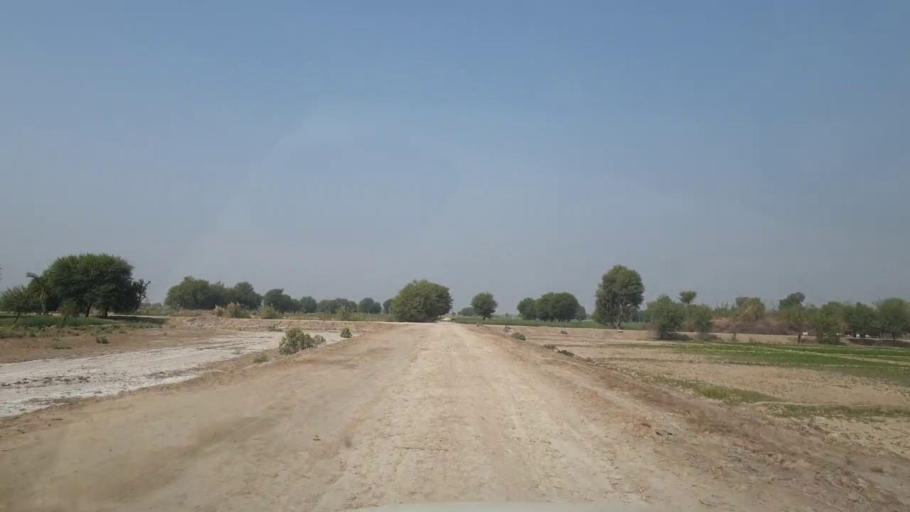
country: PK
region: Sindh
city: Mirpur Khas
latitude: 25.6575
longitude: 69.1338
